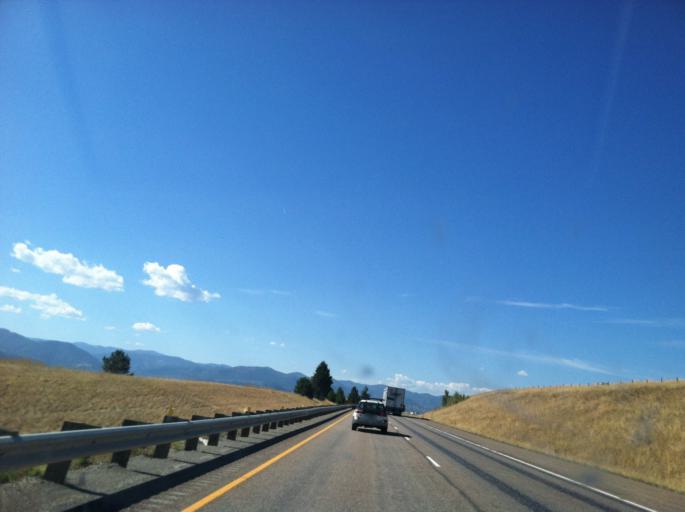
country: US
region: Montana
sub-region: Missoula County
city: Orchard Homes
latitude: 46.9386
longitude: -114.1032
